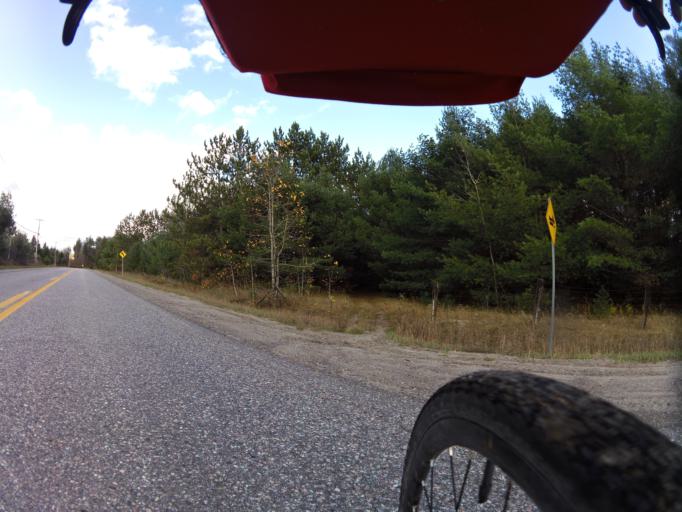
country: CA
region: Quebec
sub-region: Outaouais
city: Wakefield
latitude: 45.6807
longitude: -76.1200
